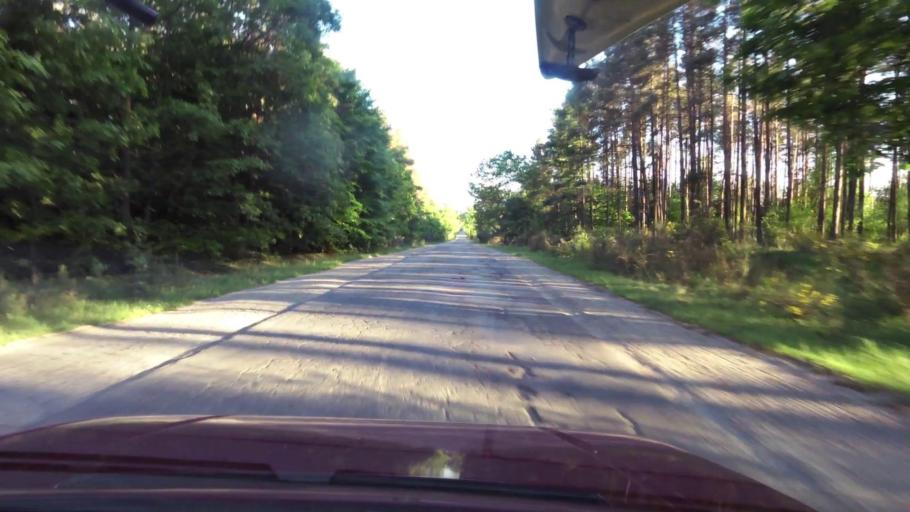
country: PL
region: West Pomeranian Voivodeship
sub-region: Powiat szczecinecki
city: Bialy Bor
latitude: 53.9220
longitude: 16.8045
